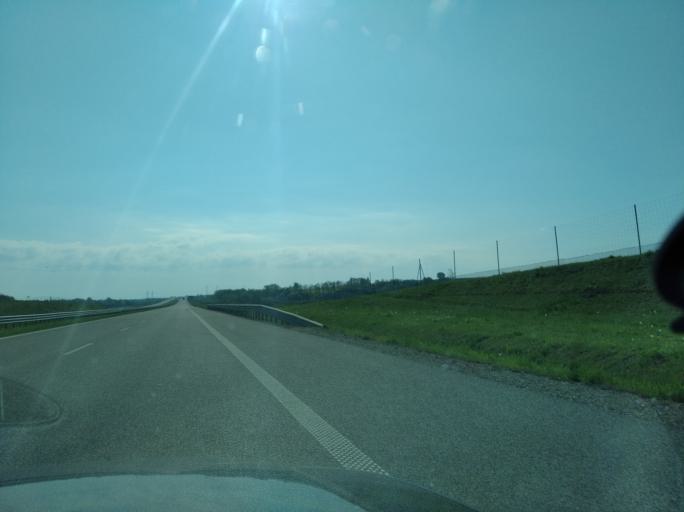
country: PL
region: Subcarpathian Voivodeship
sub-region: Powiat jaroslawski
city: Ostrow
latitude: 49.9159
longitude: 22.7700
